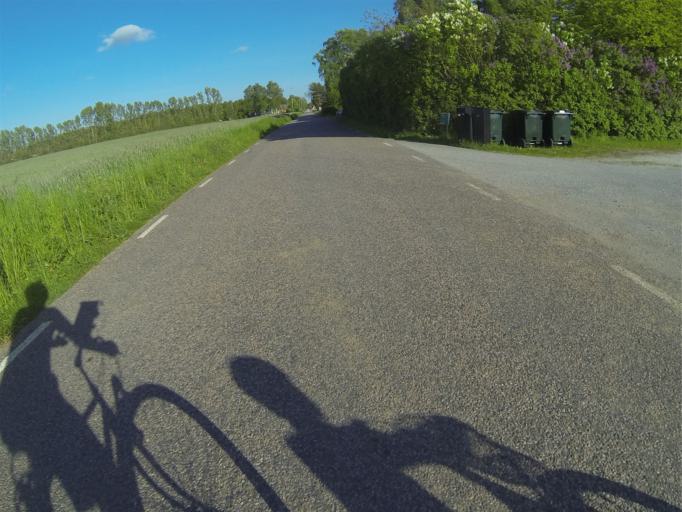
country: SE
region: Skane
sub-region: Eslovs Kommun
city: Eslov
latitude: 55.7313
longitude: 13.3778
